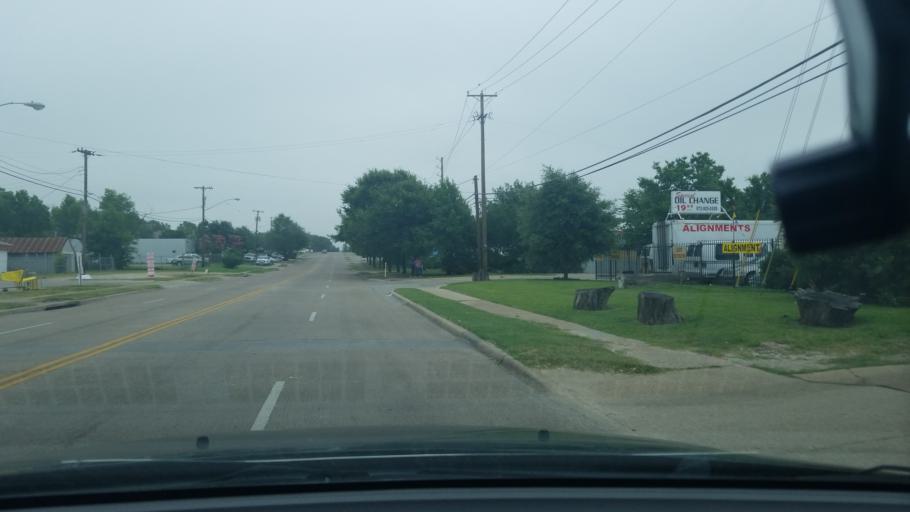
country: US
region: Texas
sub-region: Dallas County
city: Balch Springs
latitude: 32.7633
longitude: -96.6818
